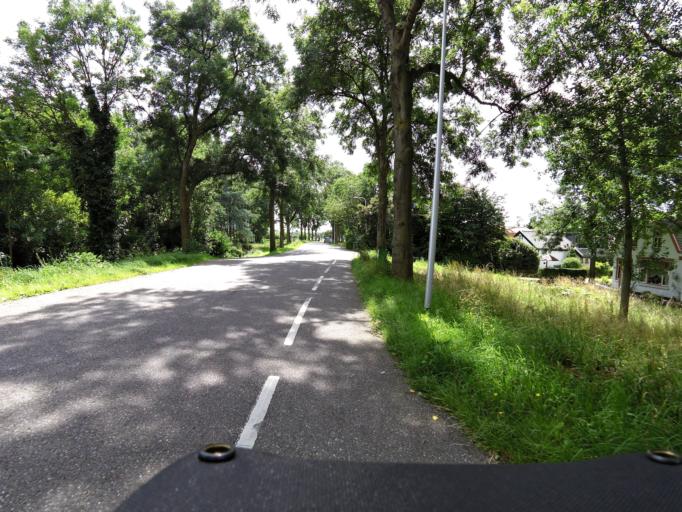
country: NL
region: South Holland
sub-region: Gemeente Albrandswaard
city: Rhoon
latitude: 51.8688
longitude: 4.4109
